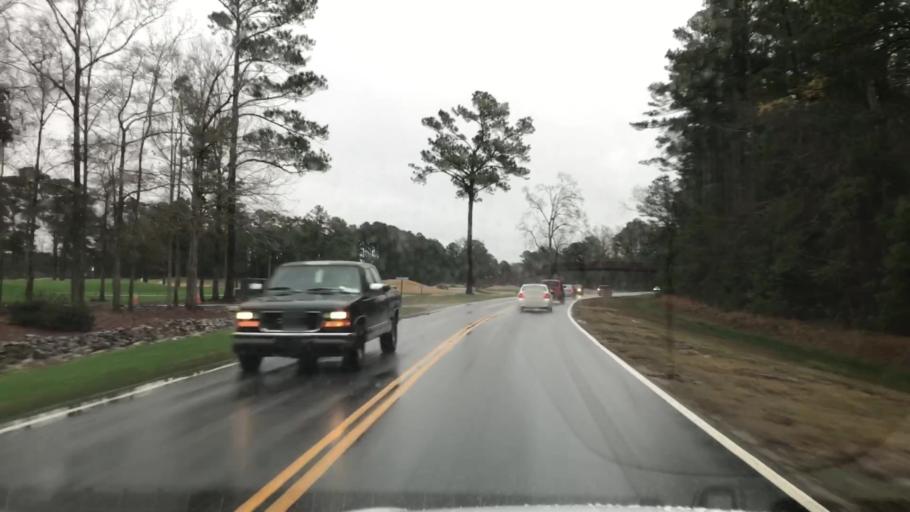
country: US
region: South Carolina
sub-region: Horry County
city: Forestbrook
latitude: 33.7272
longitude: -78.9160
